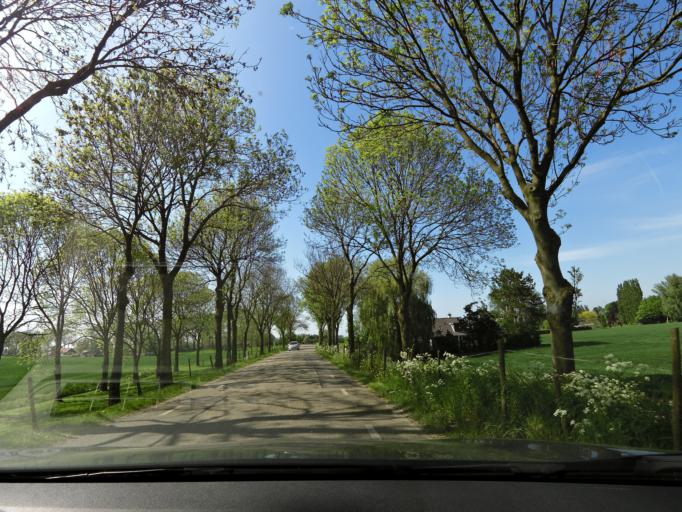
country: NL
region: South Holland
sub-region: Gemeente Binnenmaas
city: Heinenoord
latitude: 51.8499
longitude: 4.4601
